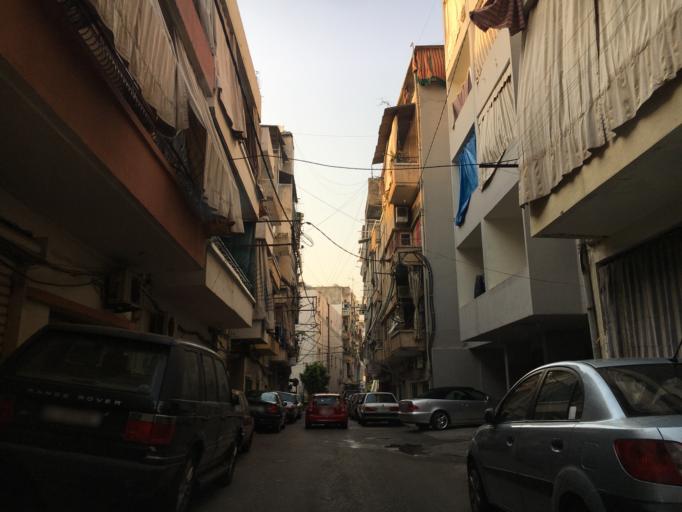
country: LB
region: Mont-Liban
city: Jdaidet el Matn
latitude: 33.8924
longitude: 35.5478
